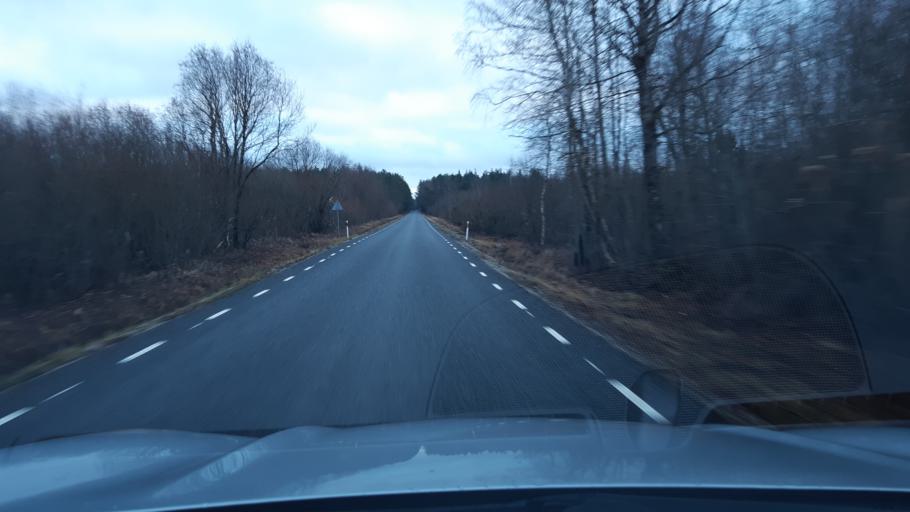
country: EE
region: Harju
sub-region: Saku vald
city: Saku
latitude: 59.1974
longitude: 24.5989
